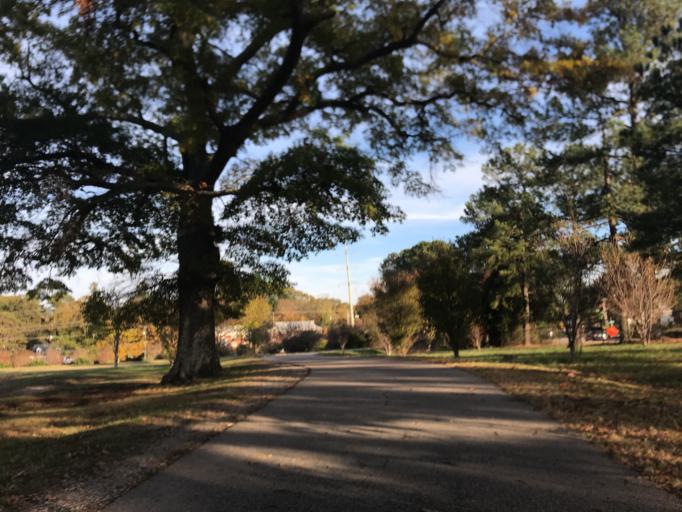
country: US
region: North Carolina
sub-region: Wake County
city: West Raleigh
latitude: 35.7943
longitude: -78.6864
